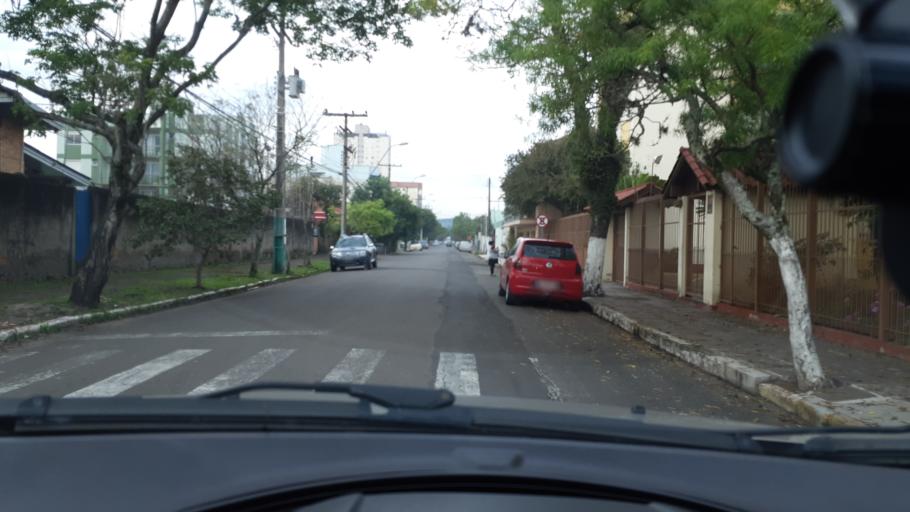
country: BR
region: Rio Grande do Sul
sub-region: Sao Leopoldo
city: Sao Leopoldo
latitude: -29.7669
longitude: -51.1519
